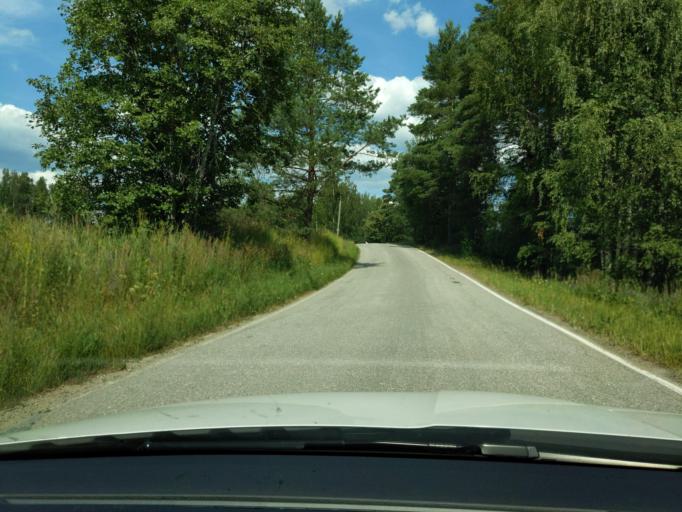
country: FI
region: Paijanne Tavastia
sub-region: Lahti
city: Heinola
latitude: 61.3394
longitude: 26.1739
